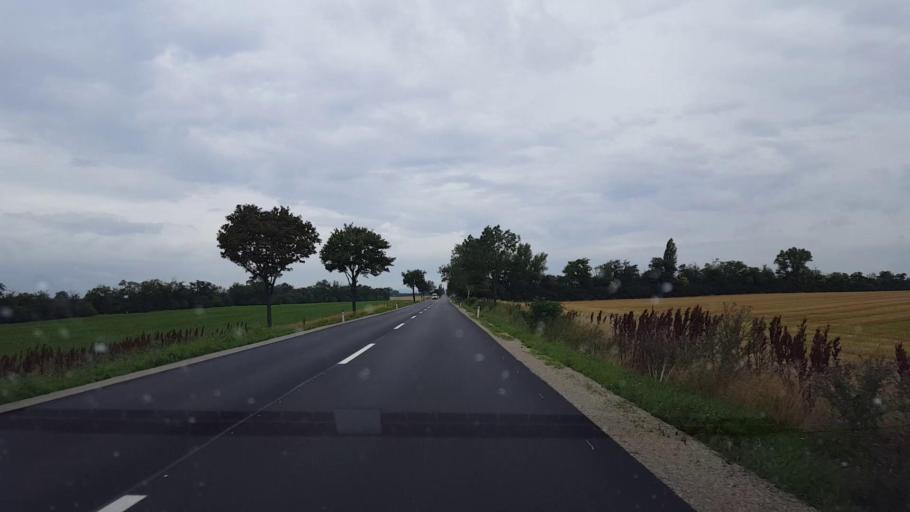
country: AT
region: Lower Austria
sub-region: Politischer Bezirk Wien-Umgebung
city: Rauchenwarth
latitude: 48.1173
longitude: 16.5162
